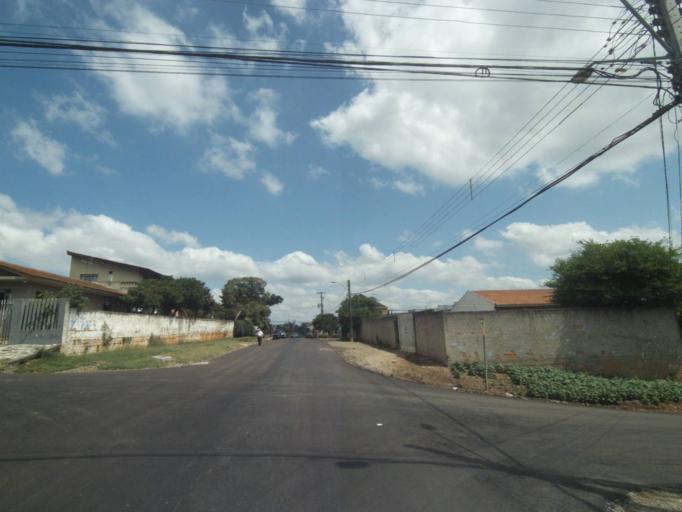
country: BR
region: Parana
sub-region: Curitiba
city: Curitiba
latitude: -25.5111
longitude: -49.3063
